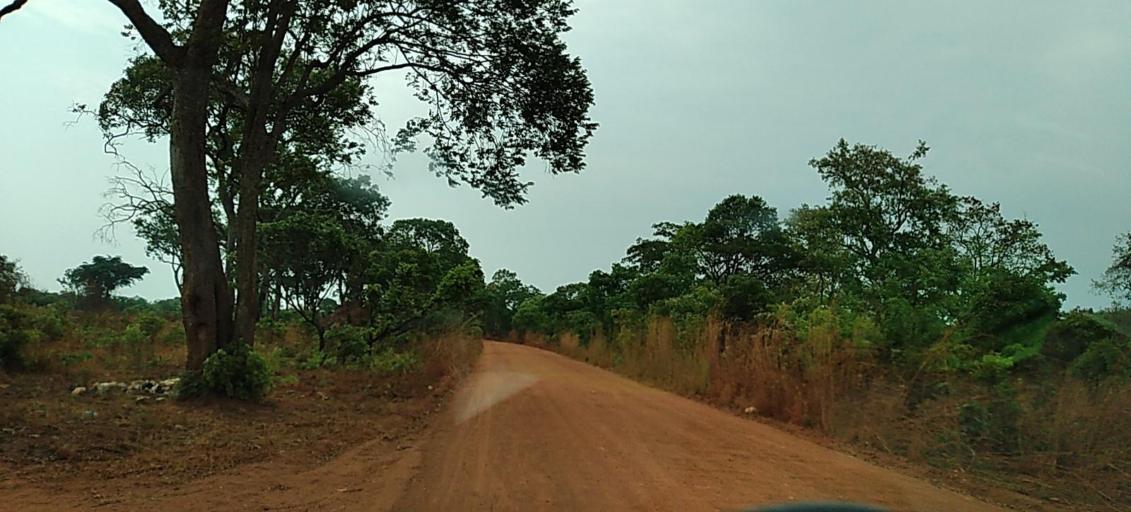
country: ZM
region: North-Western
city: Solwezi
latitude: -12.2106
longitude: 26.5020
